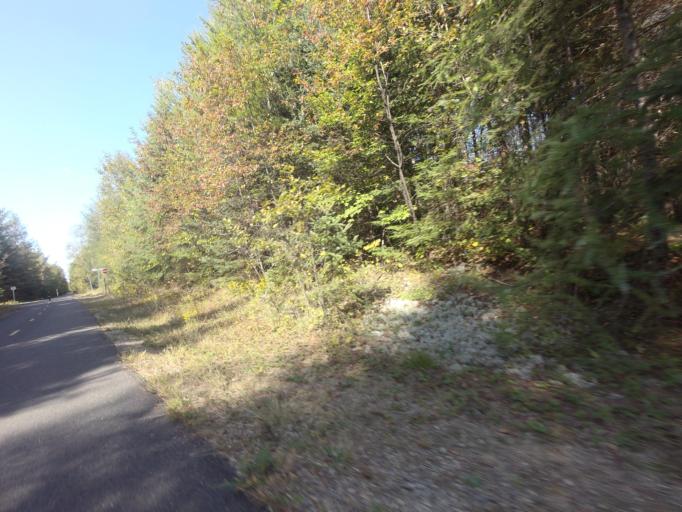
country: CA
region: Quebec
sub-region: Laurentides
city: Mont-Tremblant
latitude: 46.1227
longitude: -74.5215
